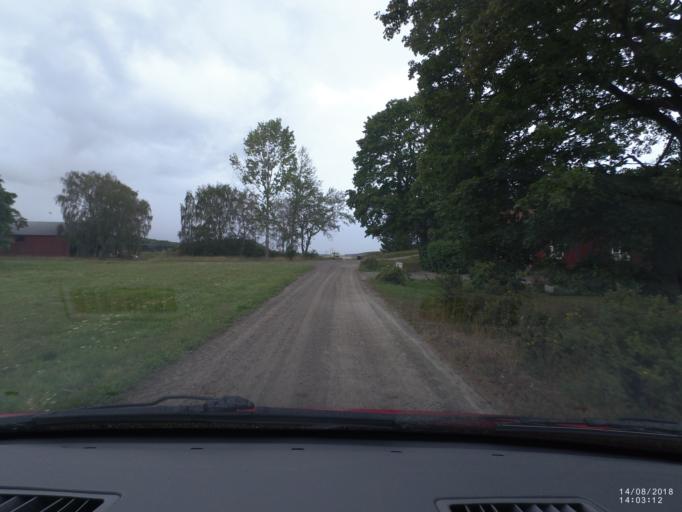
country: SE
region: Soedermanland
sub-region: Nykopings Kommun
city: Nykoping
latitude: 58.7527
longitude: 16.9630
